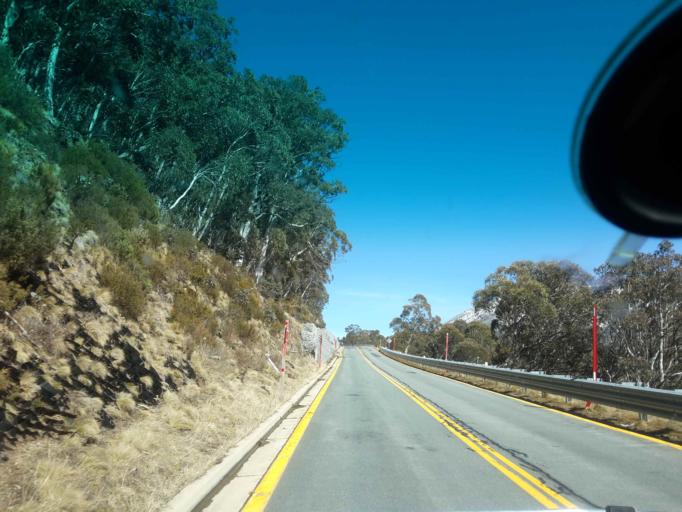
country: AU
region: New South Wales
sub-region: Snowy River
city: Jindabyne
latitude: -36.5025
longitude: 148.3124
